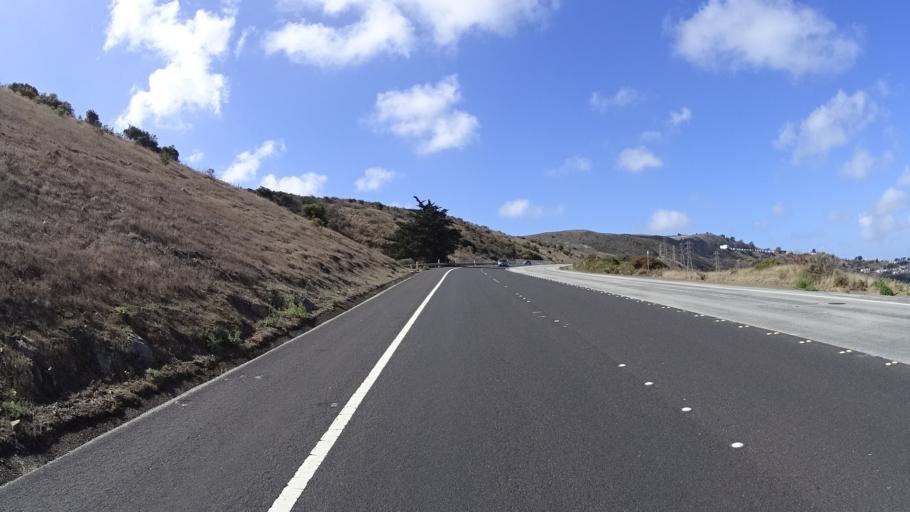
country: US
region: California
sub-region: San Mateo County
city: Brisbane
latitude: 37.6977
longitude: -122.4130
